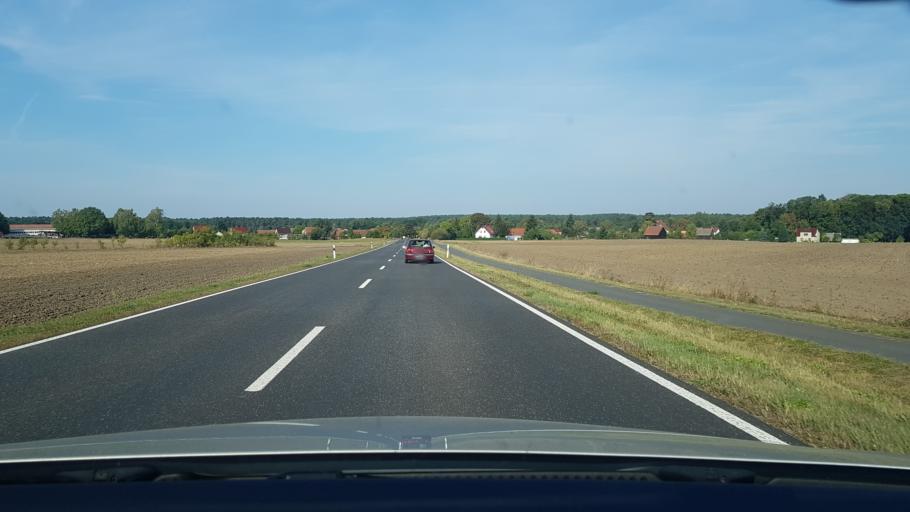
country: DE
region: Brandenburg
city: Mixdorf
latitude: 52.1392
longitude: 14.4240
